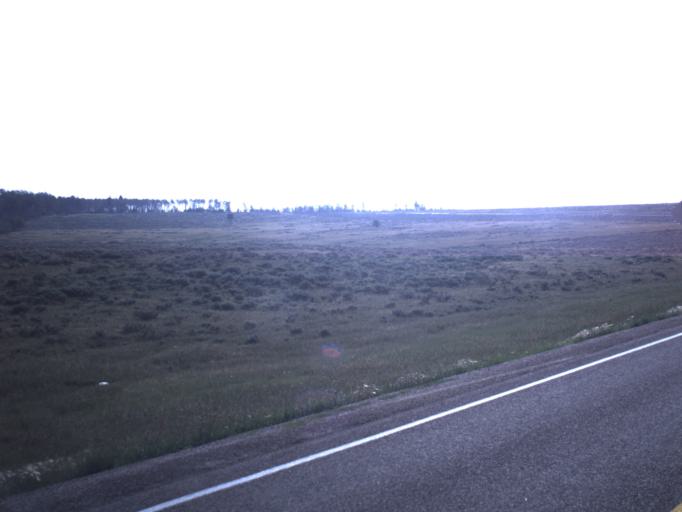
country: US
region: Utah
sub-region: Uintah County
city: Maeser
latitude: 40.7154
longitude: -109.4833
